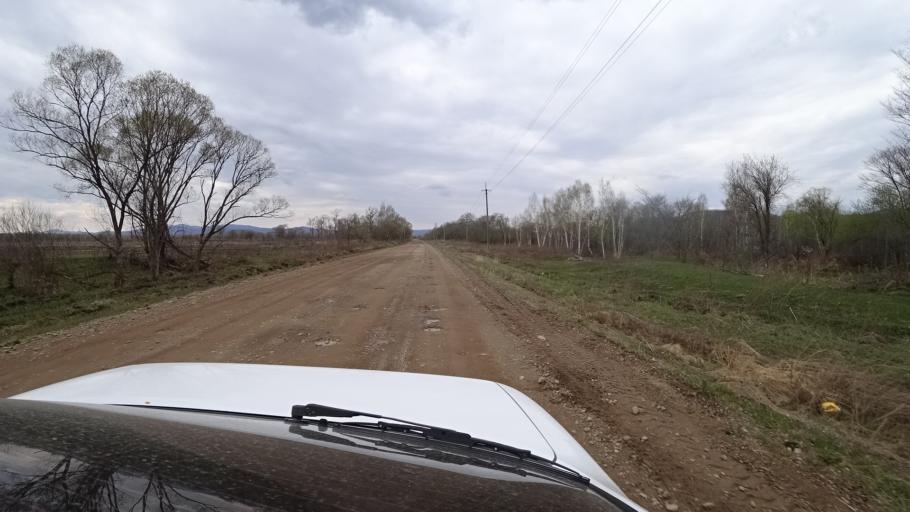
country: RU
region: Primorskiy
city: Novopokrovka
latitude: 45.5588
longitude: 134.3498
